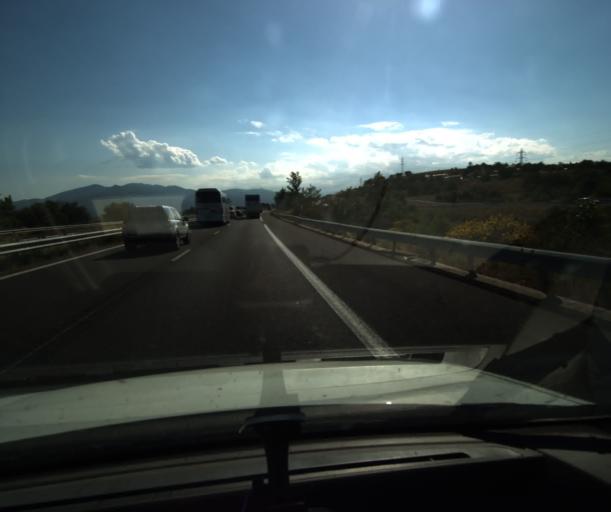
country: FR
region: Languedoc-Roussillon
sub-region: Departement des Pyrenees-Orientales
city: el Volo
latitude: 42.5395
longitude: 2.8422
